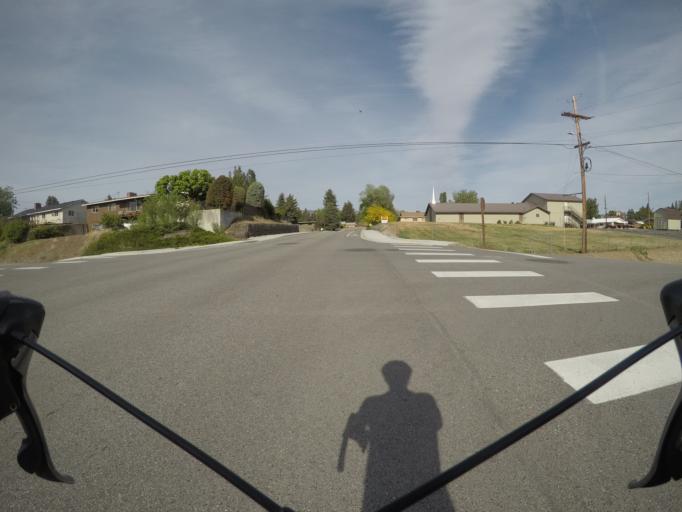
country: US
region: Washington
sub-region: Douglas County
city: East Wenatchee
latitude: 47.4121
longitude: -120.2855
